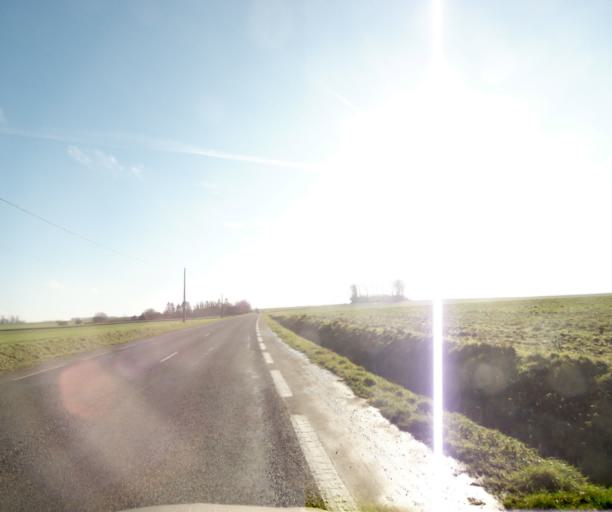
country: FR
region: Nord-Pas-de-Calais
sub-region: Departement du Nord
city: Preseau
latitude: 50.3251
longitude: 3.5625
